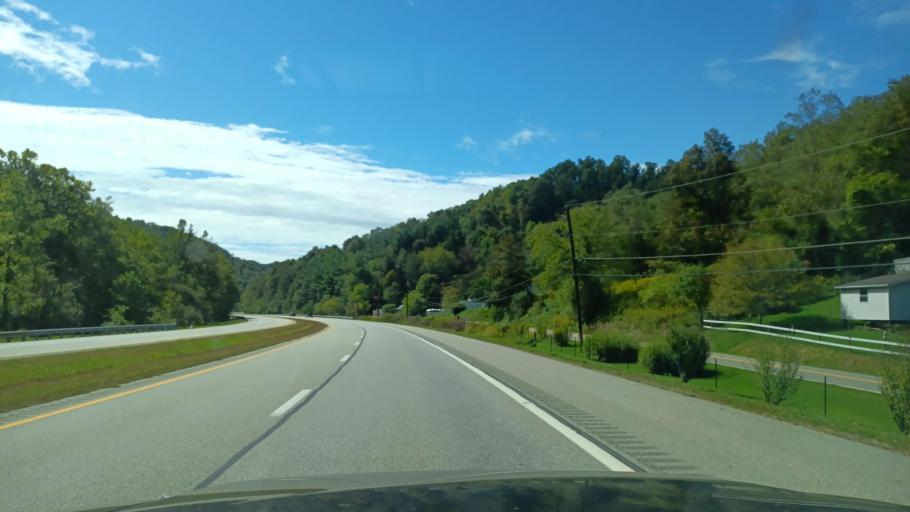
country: US
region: West Virginia
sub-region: Harrison County
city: Salem
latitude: 39.2931
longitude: -80.6327
